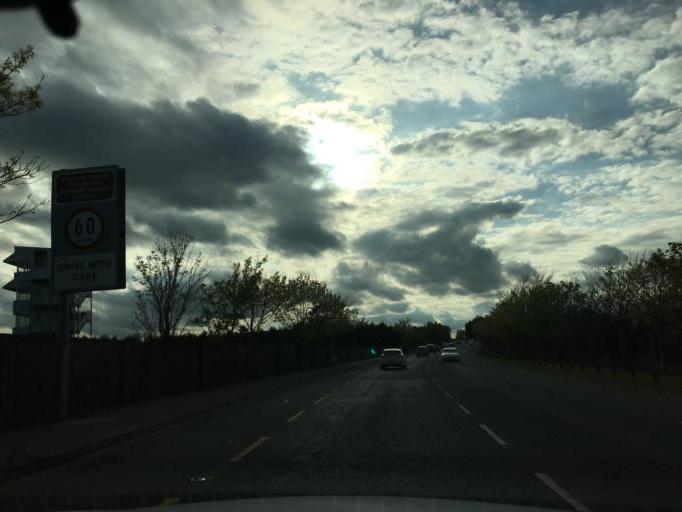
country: IE
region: Leinster
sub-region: Loch Garman
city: Loch Garman
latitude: 52.3412
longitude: -6.4930
